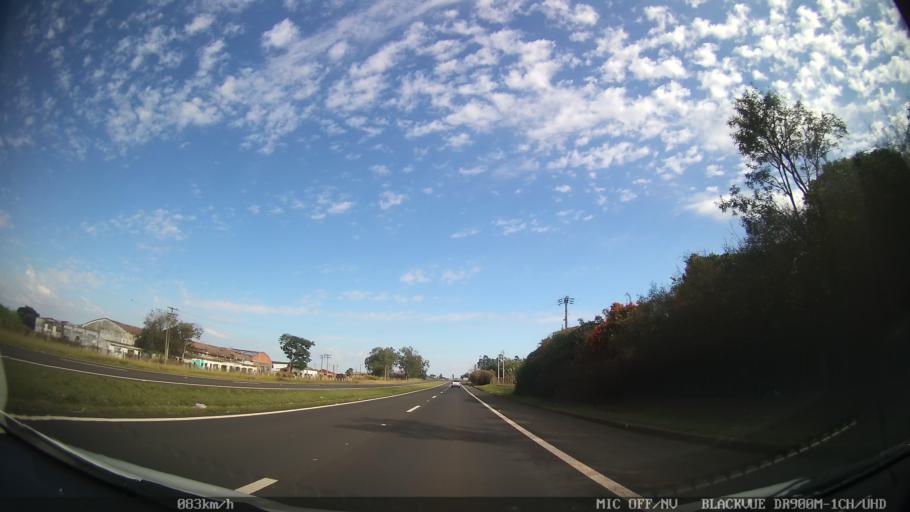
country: BR
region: Sao Paulo
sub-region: Iracemapolis
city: Iracemapolis
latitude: -22.6037
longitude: -47.4741
